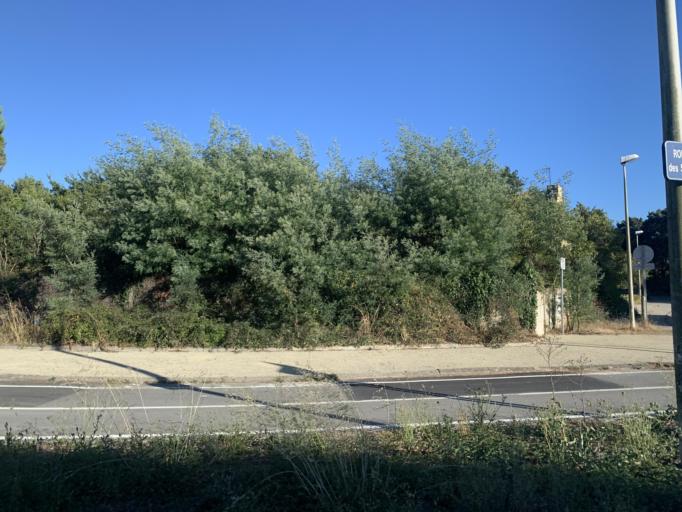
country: FR
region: Pays de la Loire
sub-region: Departement de la Loire-Atlantique
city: Pornichet
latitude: 47.2592
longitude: -2.2818
